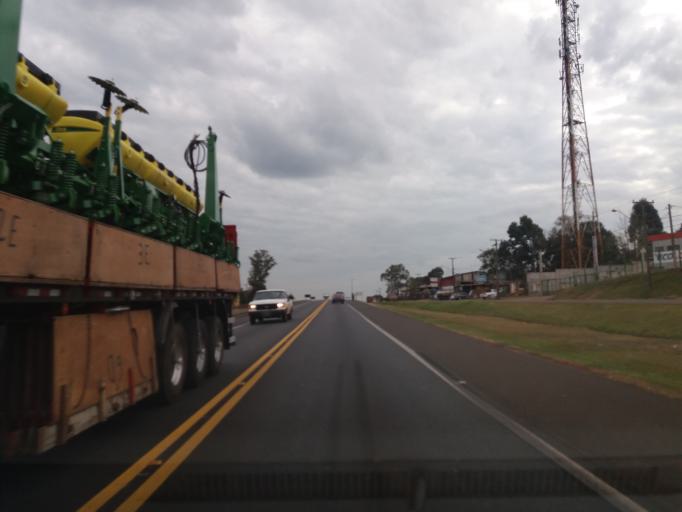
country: BR
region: Parana
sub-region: Cascavel
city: Cascavel
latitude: -24.9831
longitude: -53.4608
